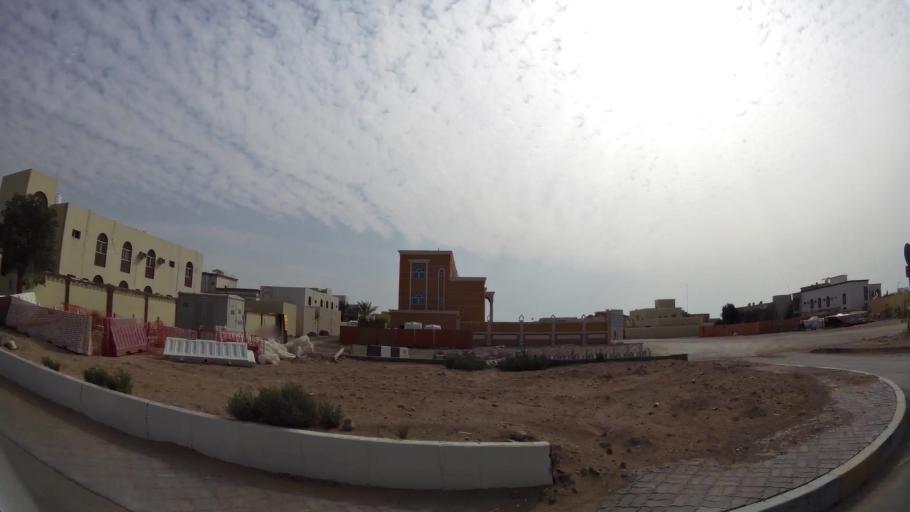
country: AE
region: Abu Dhabi
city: Abu Dhabi
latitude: 24.6049
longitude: 54.7049
